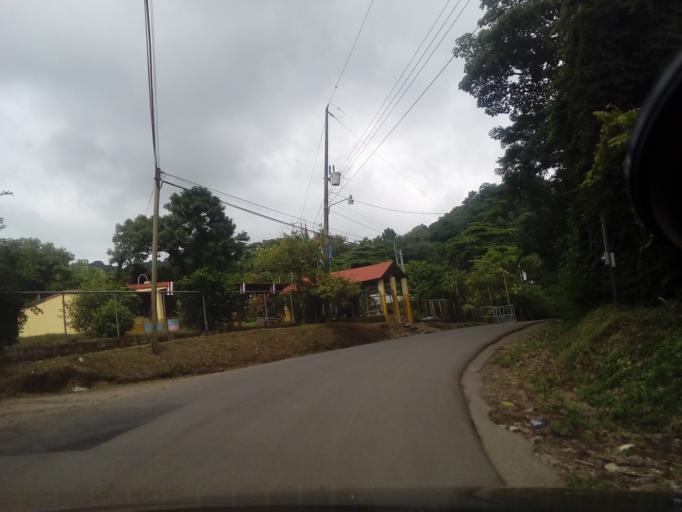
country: CR
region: Guanacaste
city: Samara
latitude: 9.9208
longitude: -85.5359
